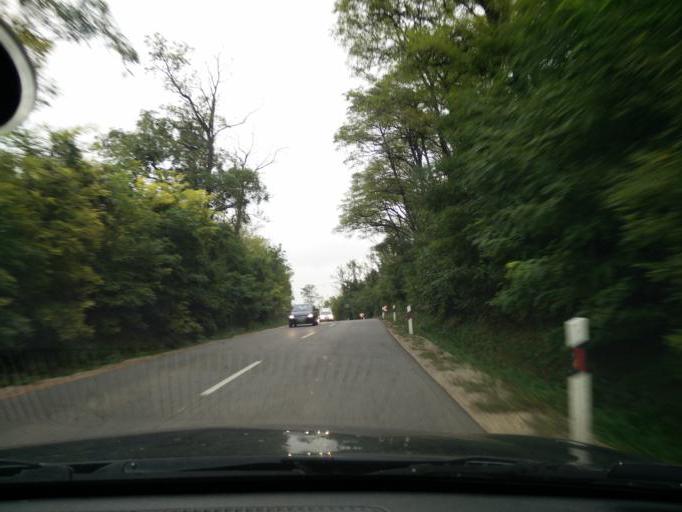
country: HU
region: Komarom-Esztergom
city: Bajna
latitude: 47.6714
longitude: 18.6044
